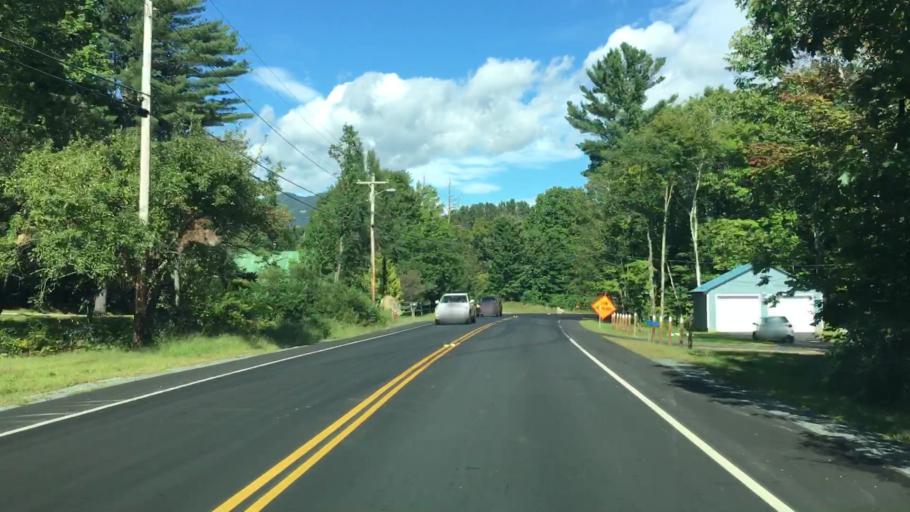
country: US
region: New Hampshire
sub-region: Grafton County
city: Woodstock
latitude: 44.0322
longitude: -71.7001
